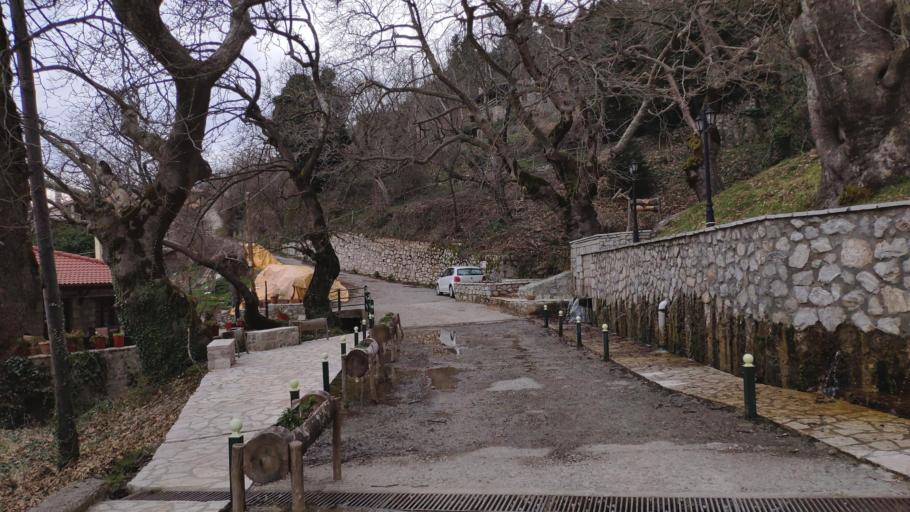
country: GR
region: Central Greece
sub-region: Nomos Fokidos
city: Amfissa
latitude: 38.6414
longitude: 22.4253
